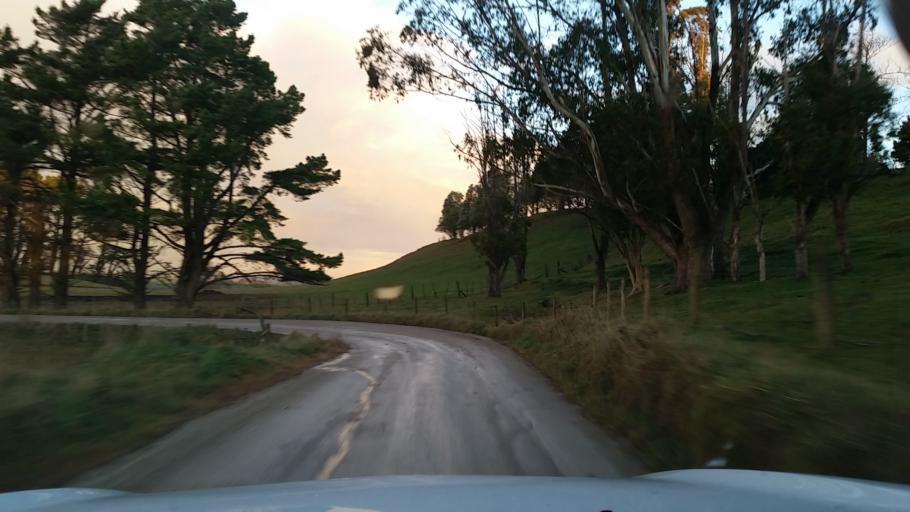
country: NZ
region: Manawatu-Wanganui
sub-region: Wanganui District
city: Wanganui
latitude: -39.7735
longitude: 174.8660
